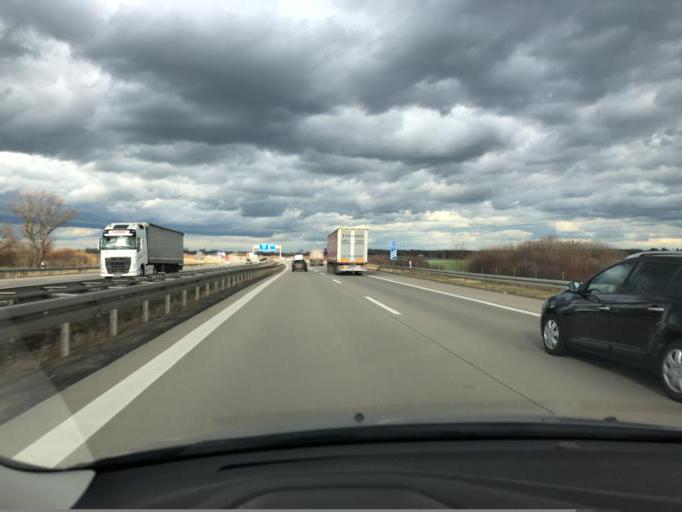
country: DE
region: Saxony
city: Naunhof
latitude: 51.3030
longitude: 12.5466
